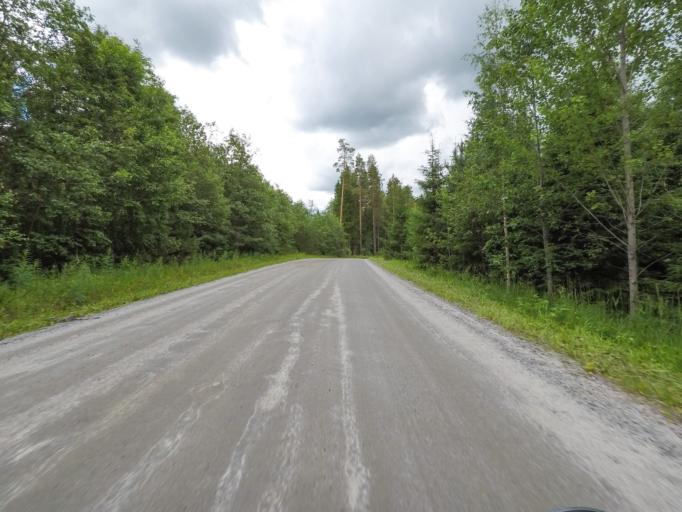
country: FI
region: Central Finland
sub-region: Jyvaeskylae
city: Hankasalmi
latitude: 62.4238
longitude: 26.6483
